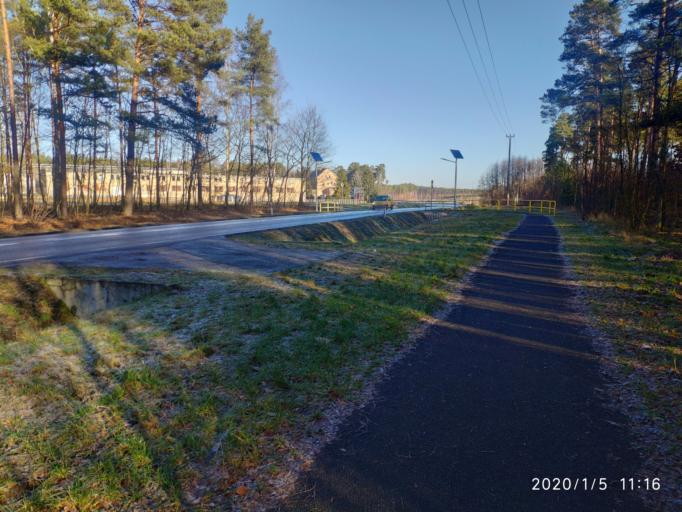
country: PL
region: Lubusz
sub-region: Powiat zielonogorski
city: Czerwiensk
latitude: 52.0001
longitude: 15.4165
